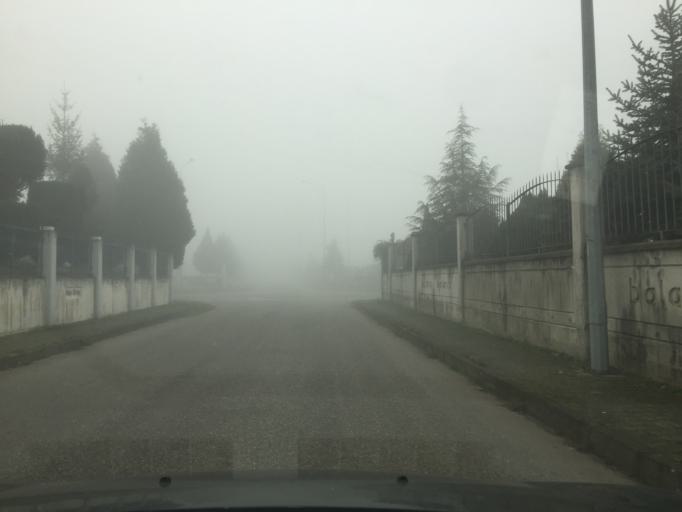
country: TR
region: Duzce
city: Duzce
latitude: 40.7860
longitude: 31.1352
